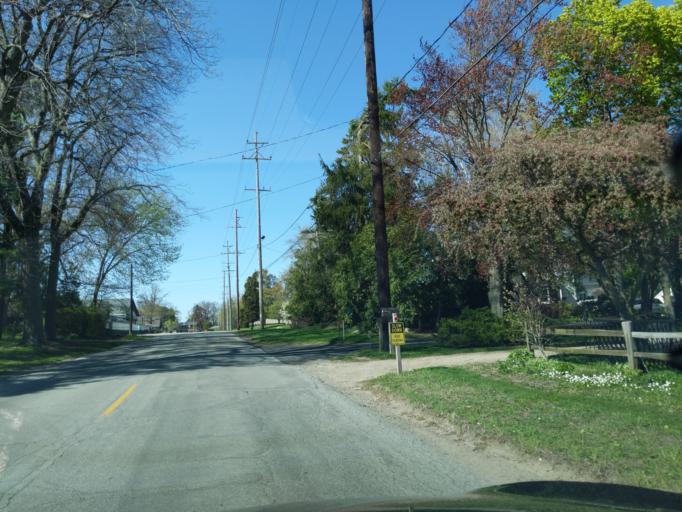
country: US
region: Michigan
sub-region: Kent County
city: East Grand Rapids
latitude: 42.9671
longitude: -85.6176
